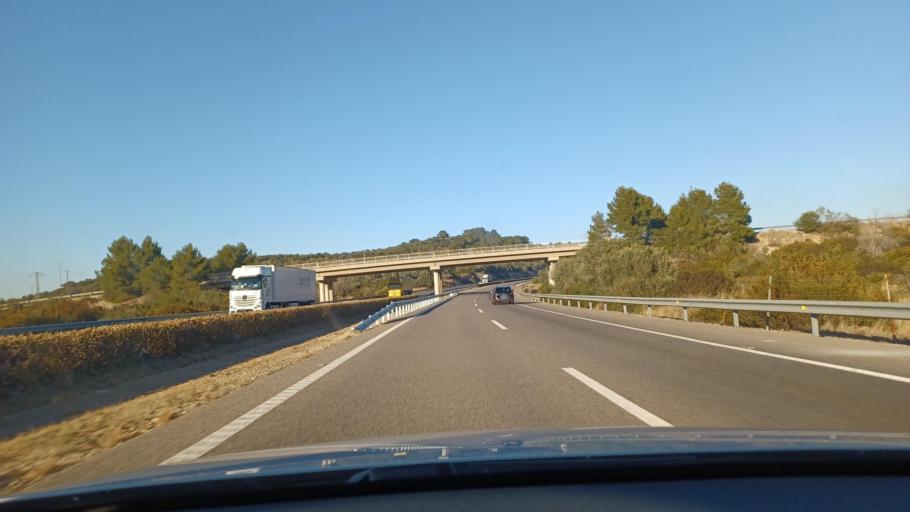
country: ES
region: Catalonia
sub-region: Provincia de Tarragona
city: Masdenverge
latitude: 40.6693
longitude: 0.5143
